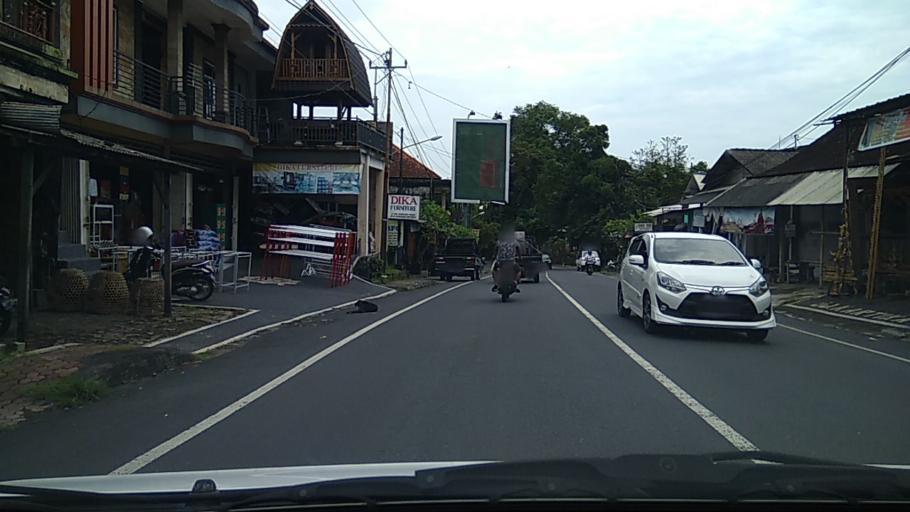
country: ID
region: Bali
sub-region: Kabupaten Gianyar
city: Ubud
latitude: -8.5352
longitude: 115.3092
